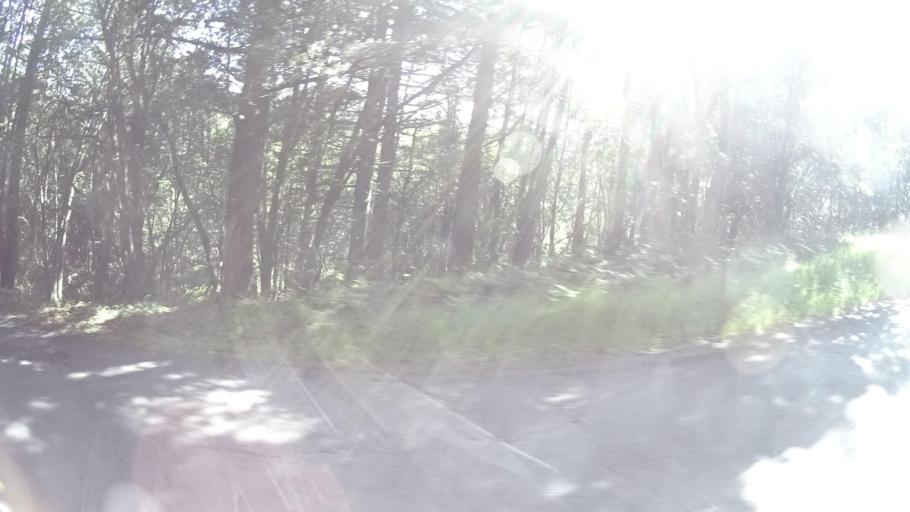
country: US
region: California
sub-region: Humboldt County
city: Rio Dell
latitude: 40.3059
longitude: -124.2583
